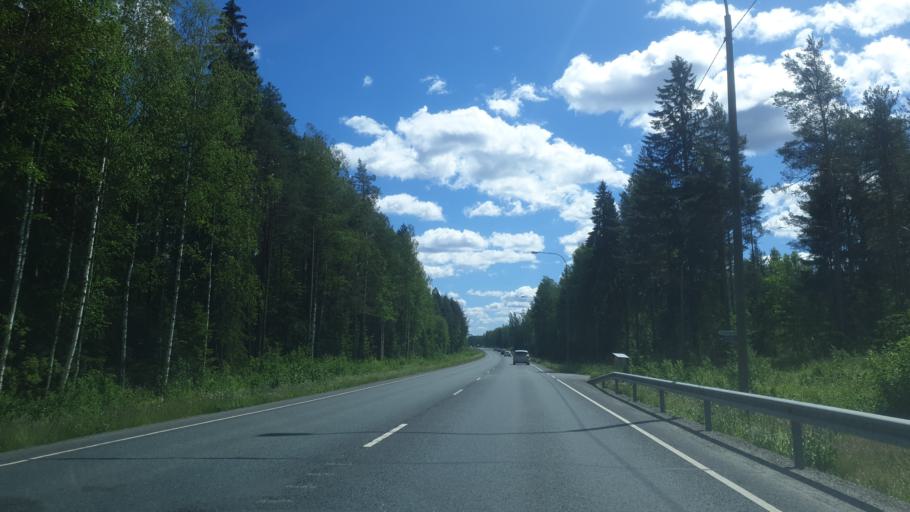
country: FI
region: Northern Savo
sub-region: Varkaus
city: Leppaevirta
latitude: 62.5248
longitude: 27.6685
